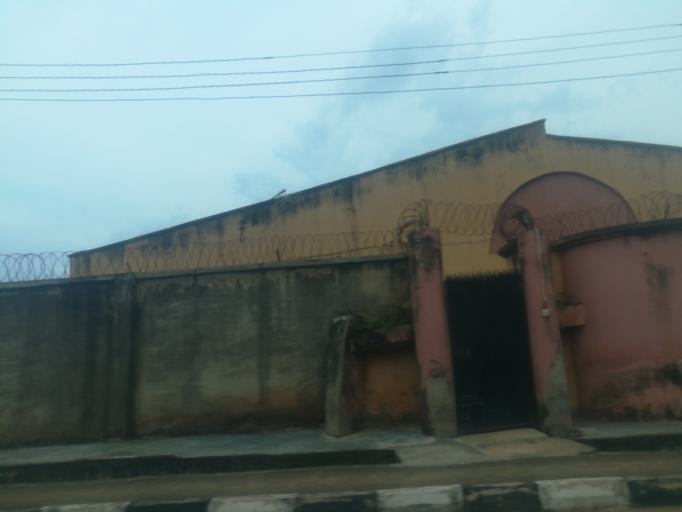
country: NG
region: Oyo
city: Ibadan
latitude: 7.3715
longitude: 3.8283
